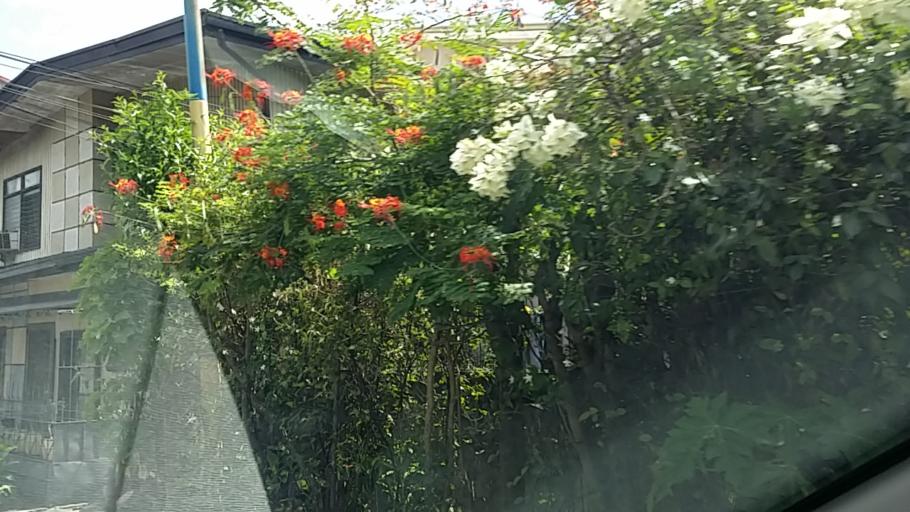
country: PH
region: Metro Manila
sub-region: Mandaluyong
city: Mandaluyong City
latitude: 14.5770
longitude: 121.0458
